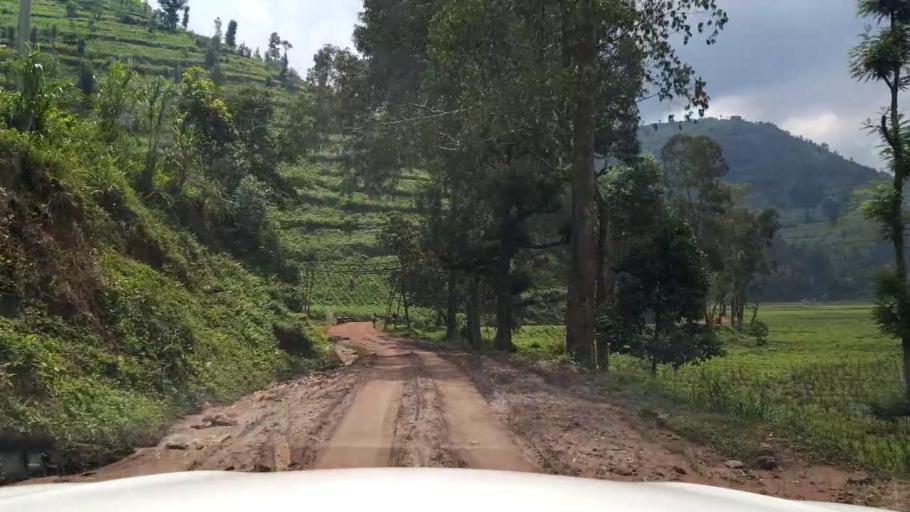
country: UG
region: Western Region
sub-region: Kisoro District
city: Kisoro
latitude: -1.3805
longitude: 29.7951
